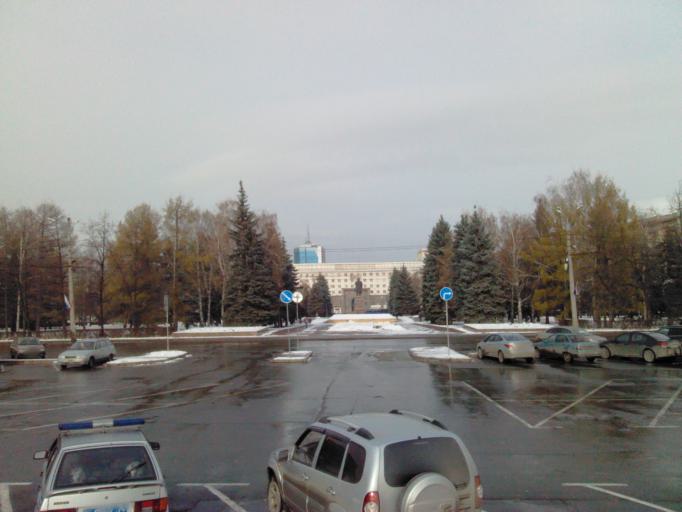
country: RU
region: Chelyabinsk
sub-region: Gorod Chelyabinsk
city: Chelyabinsk
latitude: 55.1572
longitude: 61.4028
